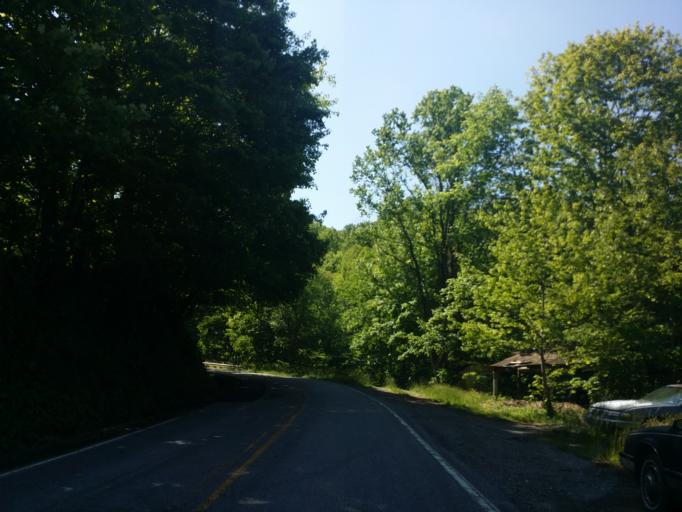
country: US
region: North Carolina
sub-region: Madison County
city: Marshall
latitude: 35.7222
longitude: -82.8400
